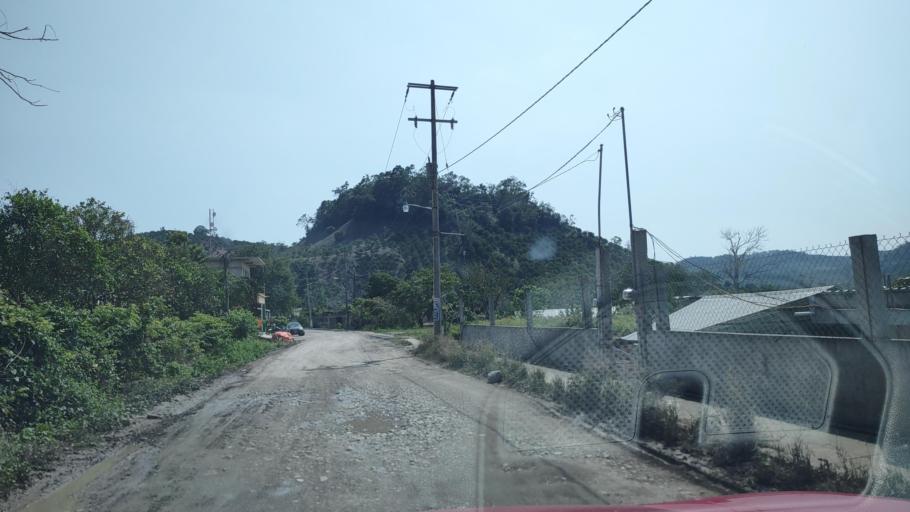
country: MX
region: Veracruz
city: Agua Dulce
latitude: 20.3177
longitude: -97.1761
